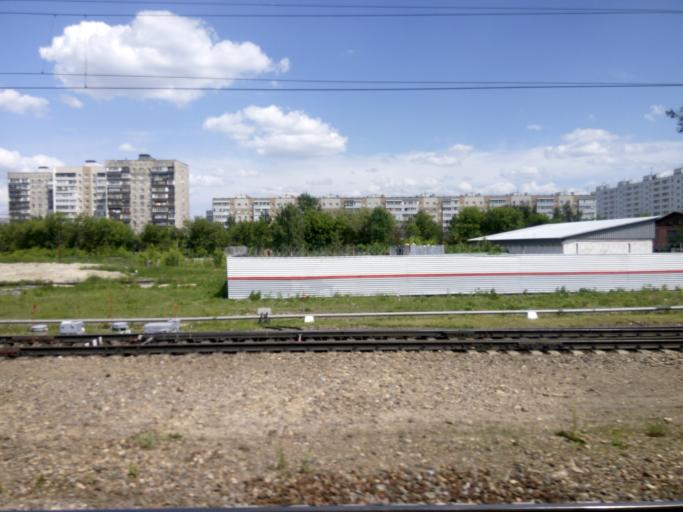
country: RU
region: Moskovskaya
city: Biryulevo Zapadnoye
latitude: 55.5991
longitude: 37.6502
